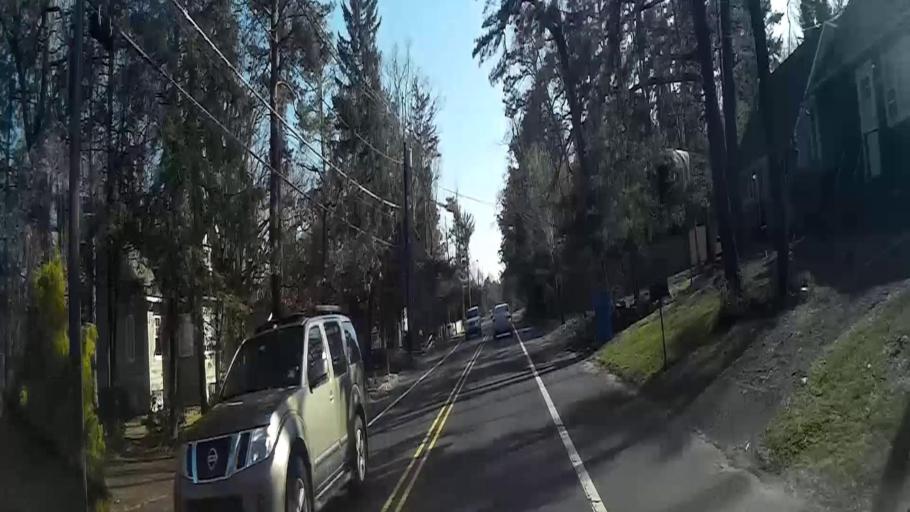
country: US
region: New Jersey
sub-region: Burlington County
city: Medford Lakes
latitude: 39.8593
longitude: -74.8543
